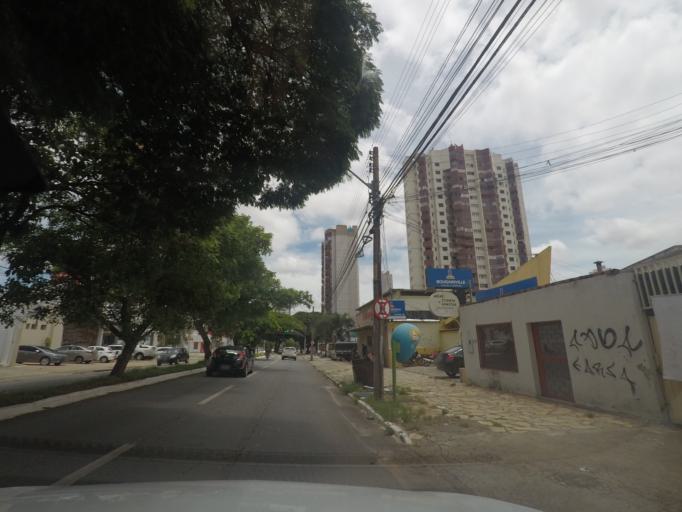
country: BR
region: Goias
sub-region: Goiania
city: Goiania
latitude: -16.6916
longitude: -49.2681
